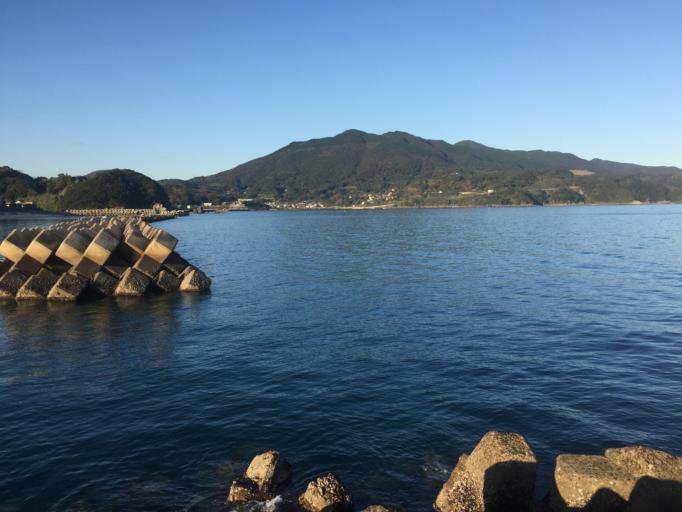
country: JP
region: Nagasaki
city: Nagasaki-shi
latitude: 32.6238
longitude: 129.8368
